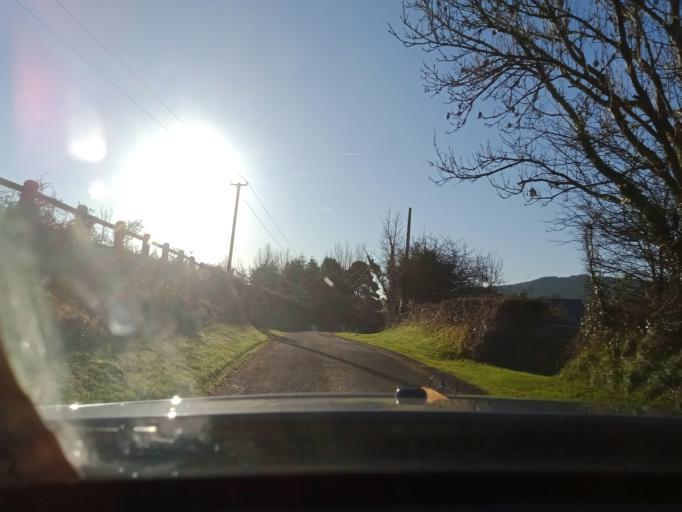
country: IE
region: Munster
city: Carrick-on-Suir
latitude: 52.4284
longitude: -7.3895
